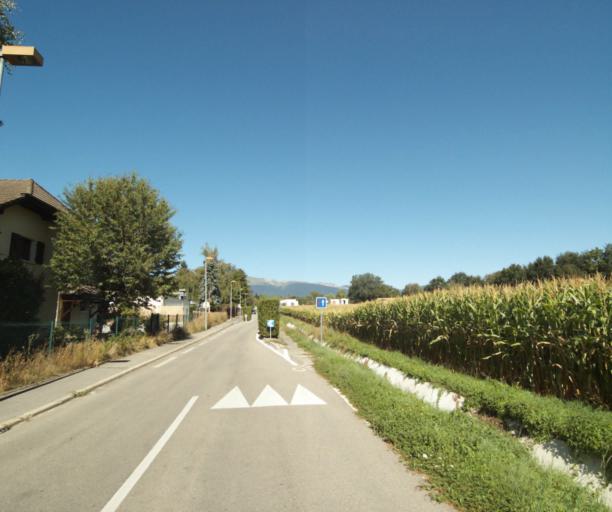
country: FR
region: Rhone-Alpes
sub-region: Departement de l'Ain
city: Ornex
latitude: 46.2609
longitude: 6.0979
